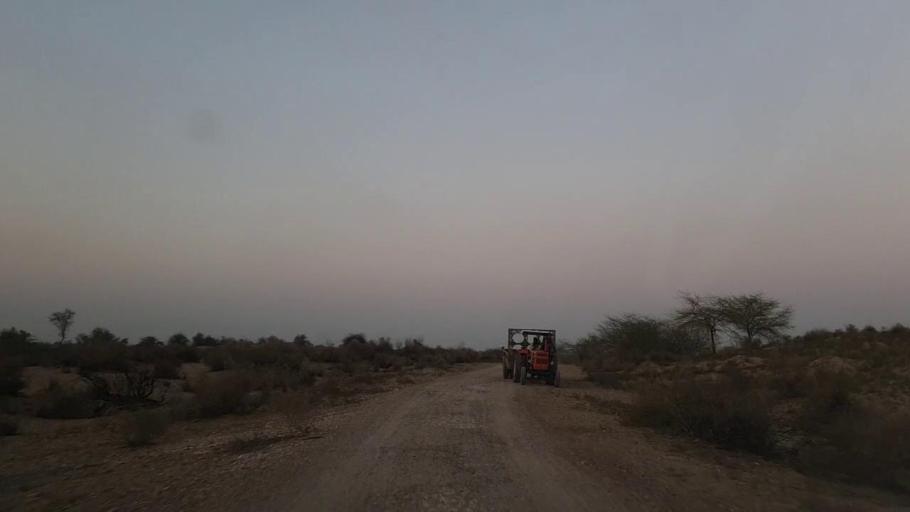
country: PK
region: Sindh
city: Bandhi
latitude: 26.6072
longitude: 68.3791
